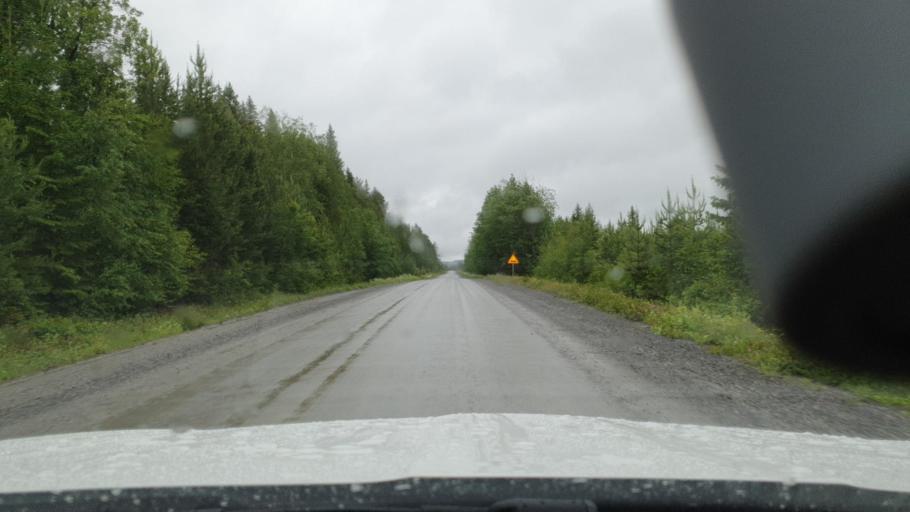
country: SE
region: Vaesterbotten
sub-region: Skelleftea Kommun
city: Burtraesk
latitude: 64.3765
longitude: 20.3556
